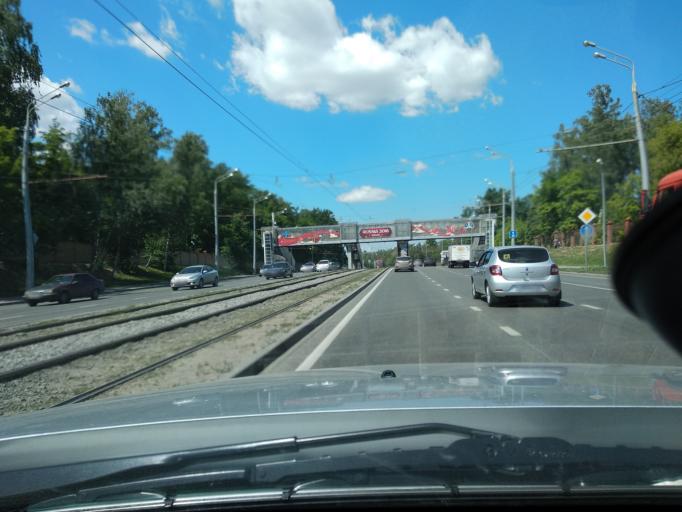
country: RU
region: Tatarstan
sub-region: Gorod Kazan'
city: Kazan
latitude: 55.8179
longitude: 49.1784
